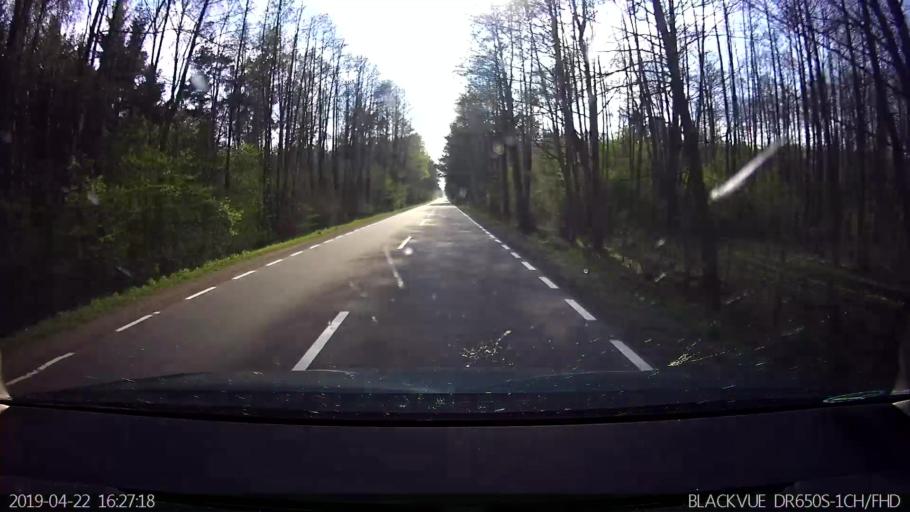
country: PL
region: Podlasie
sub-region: Powiat siemiatycki
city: Milejczyce
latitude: 52.5458
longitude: 23.2048
